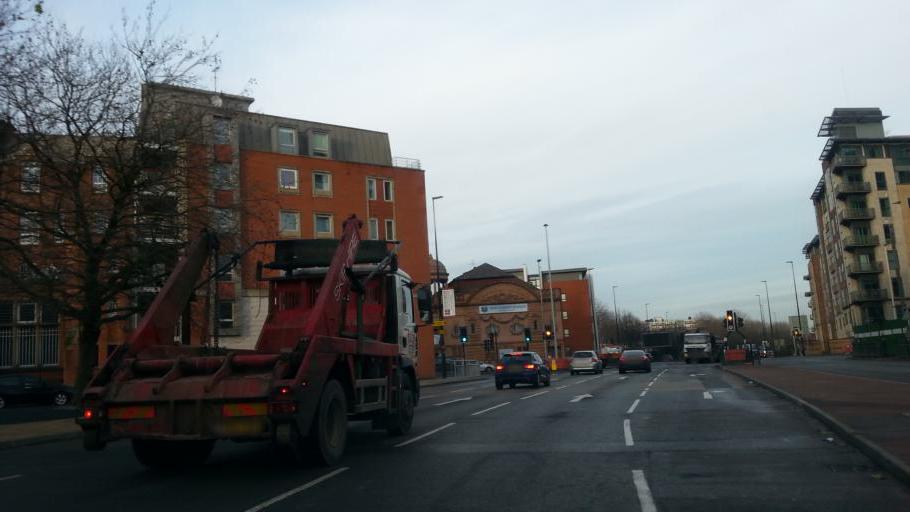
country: GB
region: England
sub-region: Manchester
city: Hulme
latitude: 53.4827
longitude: -2.2577
